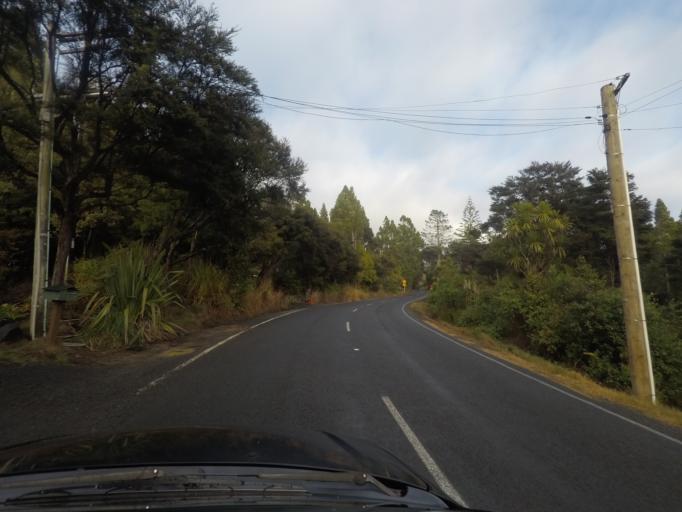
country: NZ
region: Auckland
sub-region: Auckland
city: Waitakere
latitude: -36.9158
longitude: 174.6005
